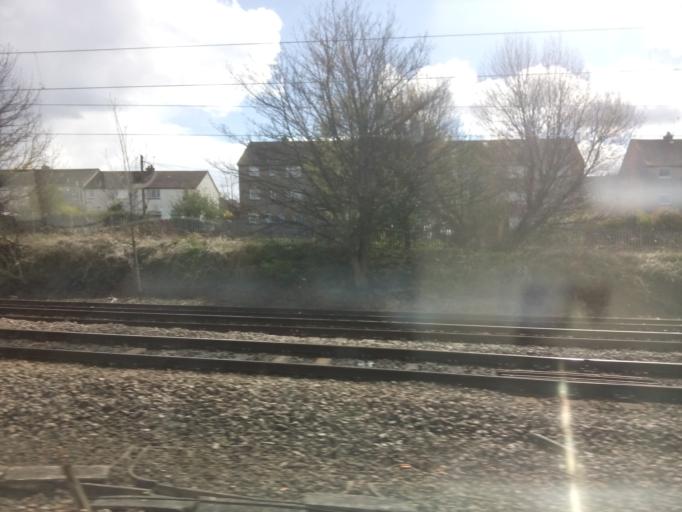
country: GB
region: Scotland
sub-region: West Lothian
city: Seafield
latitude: 55.9472
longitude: -3.1077
